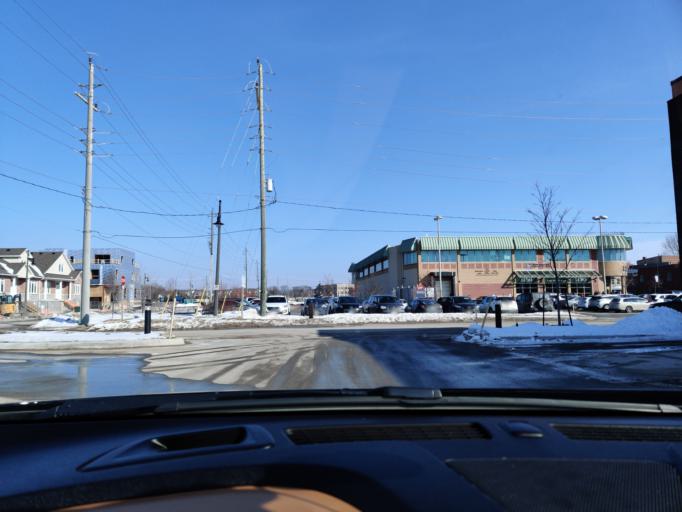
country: CA
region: Ontario
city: Collingwood
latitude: 44.5033
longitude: -80.2194
